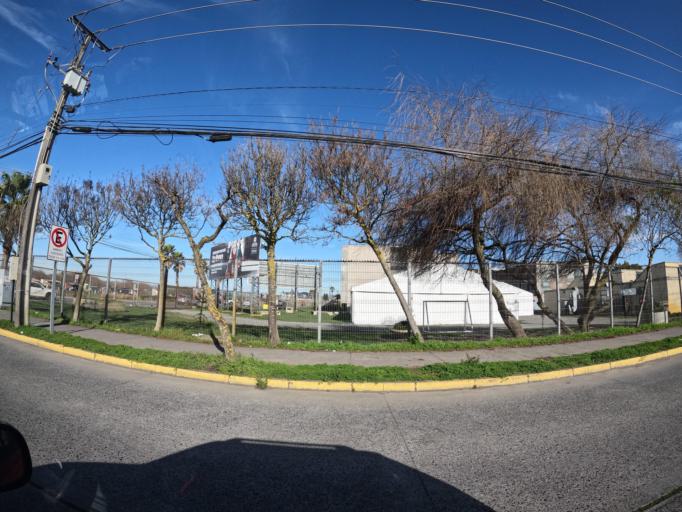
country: CL
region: Biobio
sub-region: Provincia de Concepcion
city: Concepcion
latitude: -36.7787
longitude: -73.0760
